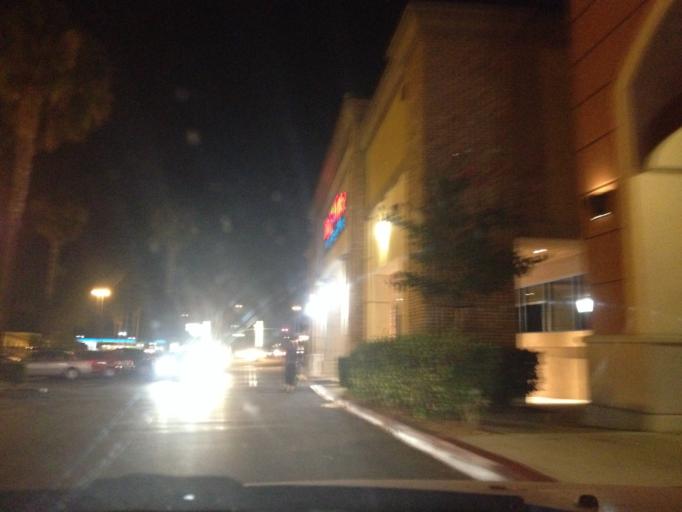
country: US
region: California
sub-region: Orange County
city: Brea
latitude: 33.9124
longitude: -117.8819
